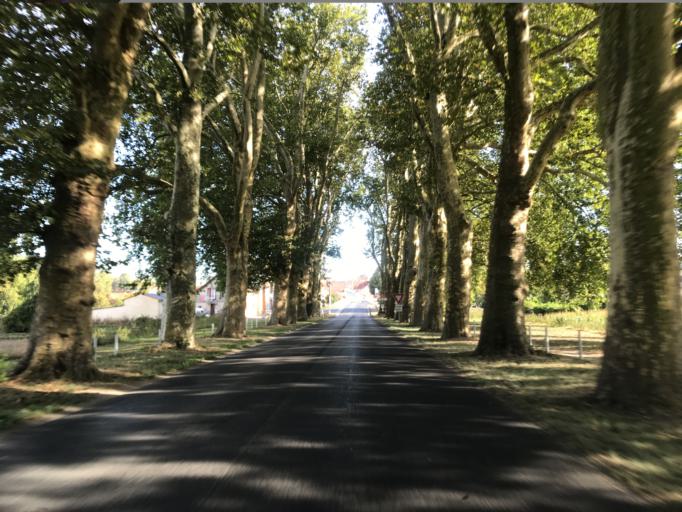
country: FR
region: Champagne-Ardenne
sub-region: Departement de la Marne
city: Damery
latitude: 49.0677
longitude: 3.8764
